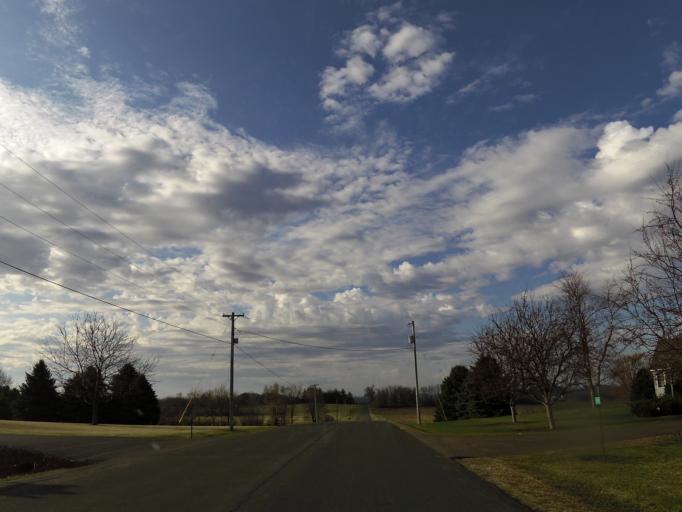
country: US
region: Minnesota
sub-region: Dakota County
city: Hastings
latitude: 44.7771
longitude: -92.8429
